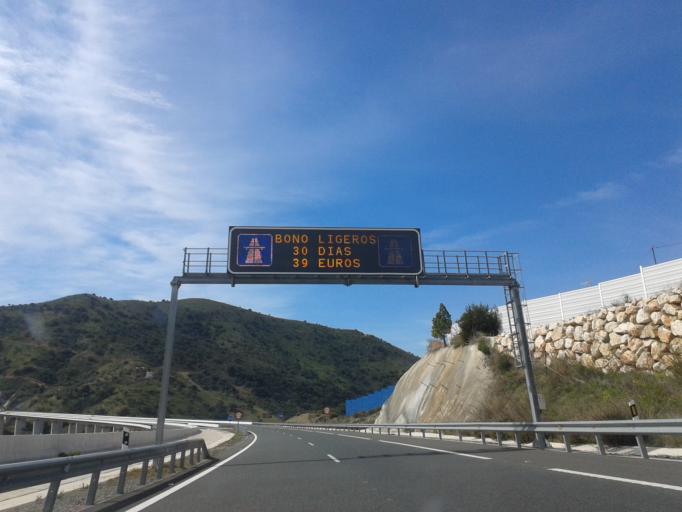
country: ES
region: Andalusia
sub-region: Provincia de Malaga
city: Casabermeja
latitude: 36.8790
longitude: -4.4792
